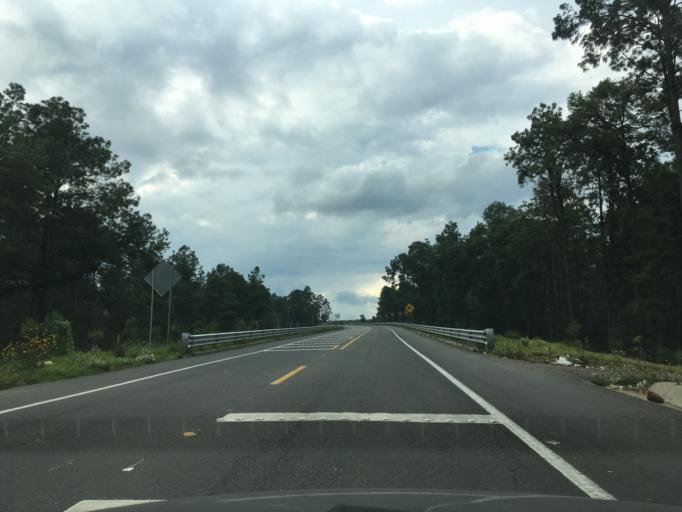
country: MX
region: Michoacan
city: Angahuan
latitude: 19.5155
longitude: -102.1721
